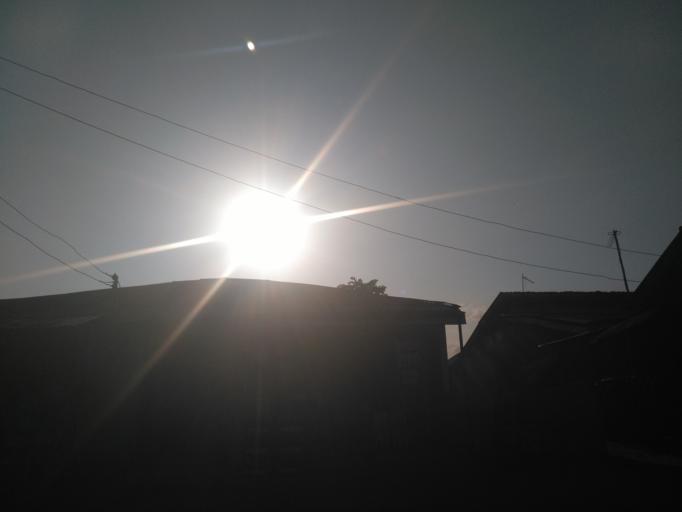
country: TZ
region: Dar es Salaam
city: Dar es Salaam
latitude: -6.9063
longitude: 39.2672
